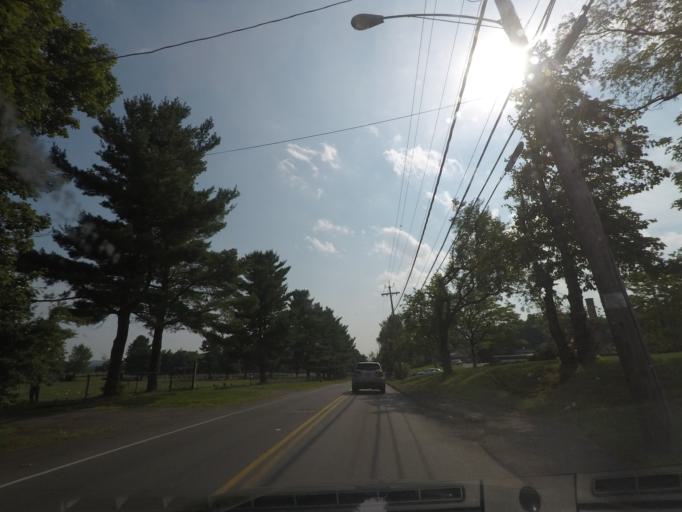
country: US
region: New York
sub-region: Rensselaer County
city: Troy
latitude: 42.7314
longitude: -73.6627
